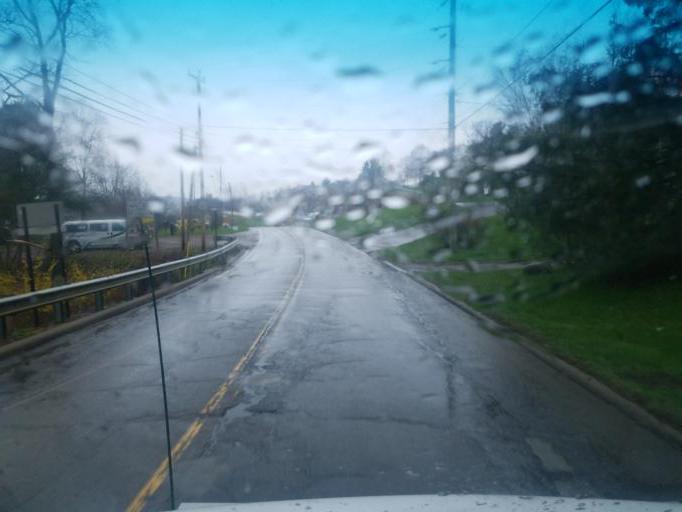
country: US
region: Ohio
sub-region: Holmes County
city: Millersburg
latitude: 40.5674
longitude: -81.9215
